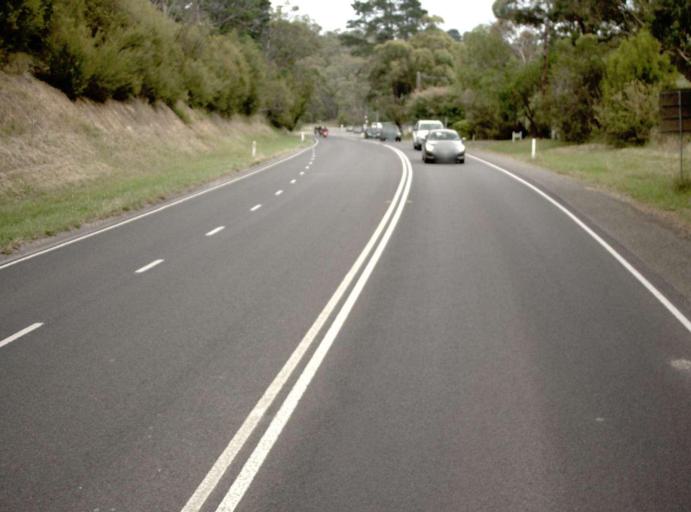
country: AU
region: Victoria
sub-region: Yarra Ranges
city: Launching Place
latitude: -37.7750
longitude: 145.5807
